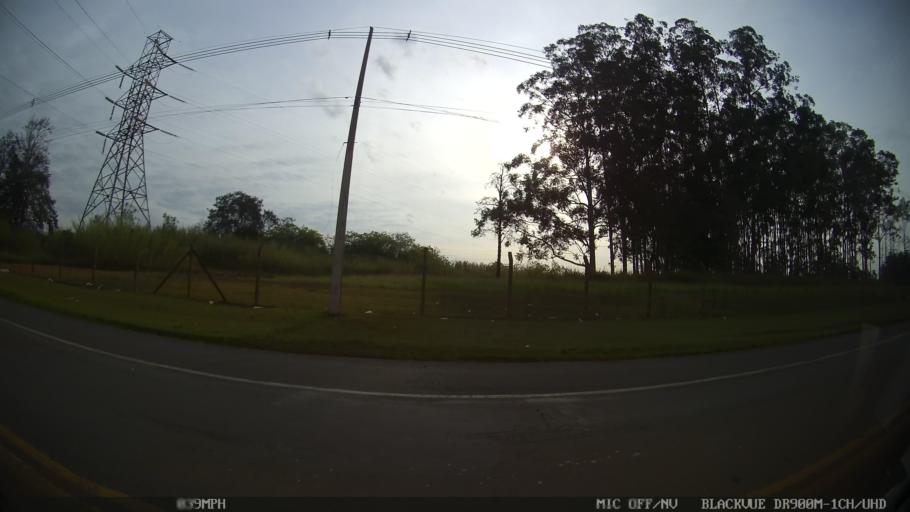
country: BR
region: Sao Paulo
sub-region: Piracicaba
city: Piracicaba
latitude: -22.7204
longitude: -47.5834
